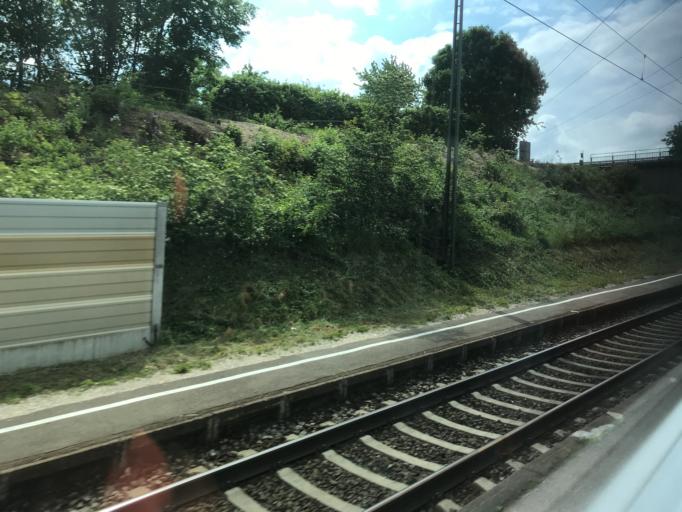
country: DE
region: Baden-Wuerttemberg
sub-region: Tuebingen Region
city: Beimerstetten
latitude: 48.4808
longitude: 9.9768
